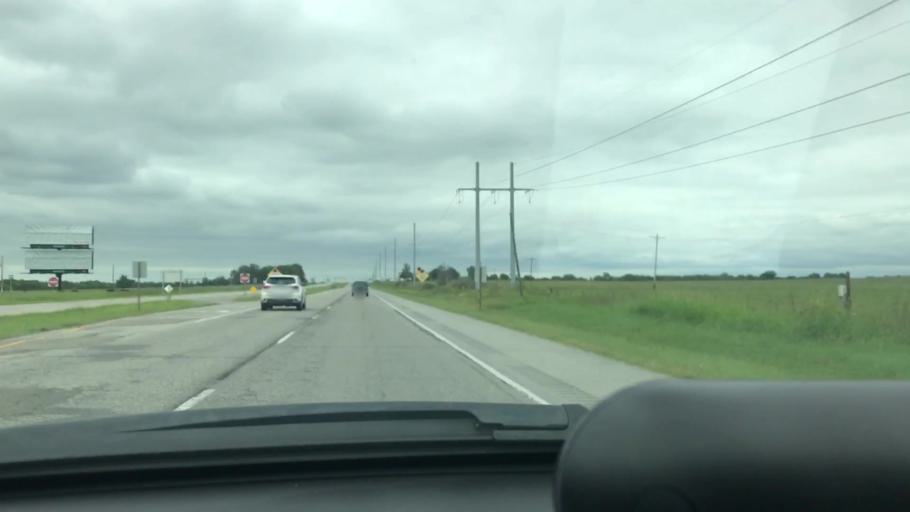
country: US
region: Oklahoma
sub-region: Wagoner County
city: Wagoner
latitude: 36.0093
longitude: -95.3685
